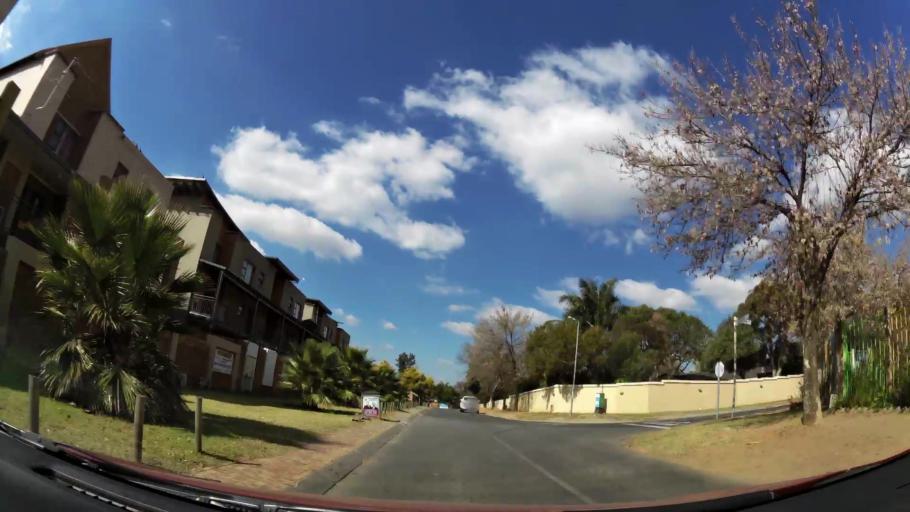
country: ZA
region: Gauteng
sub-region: City of Johannesburg Metropolitan Municipality
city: Roodepoort
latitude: -26.0725
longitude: 27.9687
